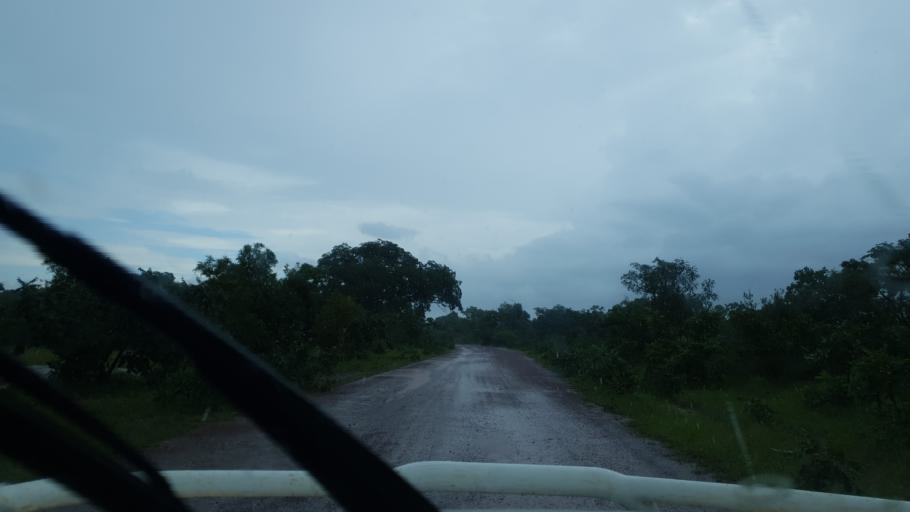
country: ML
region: Sikasso
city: Kolondieba
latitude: 11.6005
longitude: -6.6699
